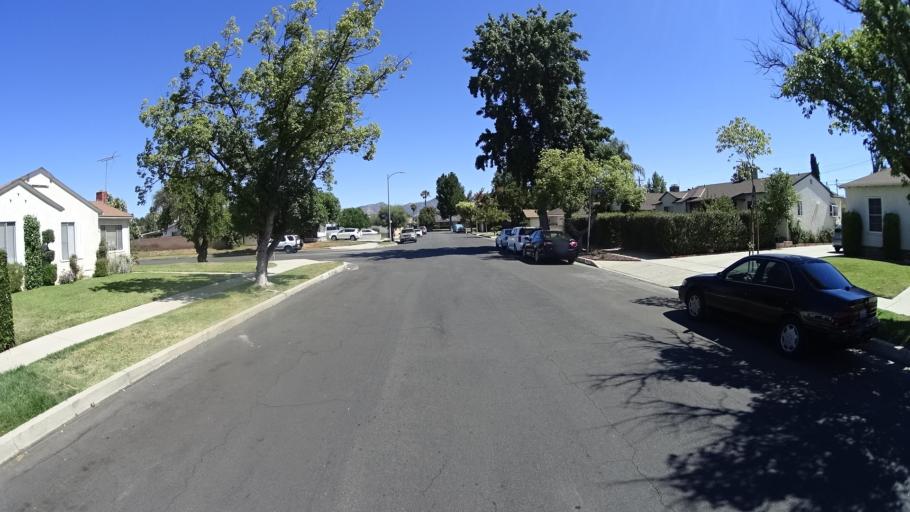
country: US
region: California
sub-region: Los Angeles County
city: San Fernando
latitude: 34.2551
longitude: -118.4630
